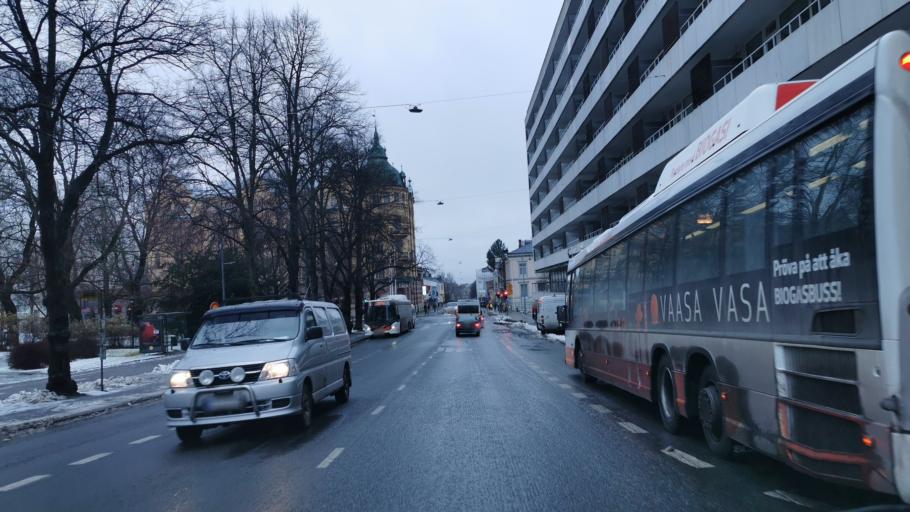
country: FI
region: Ostrobothnia
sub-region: Vaasa
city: Vaasa
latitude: 63.0950
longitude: 21.6134
